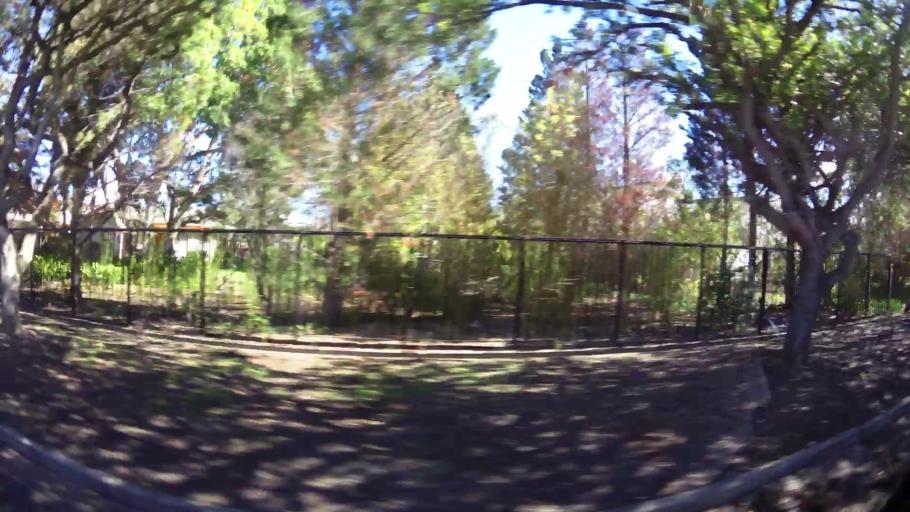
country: ZA
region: Western Cape
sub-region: Cape Winelands District Municipality
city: Ashton
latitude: -33.8068
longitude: 19.8977
